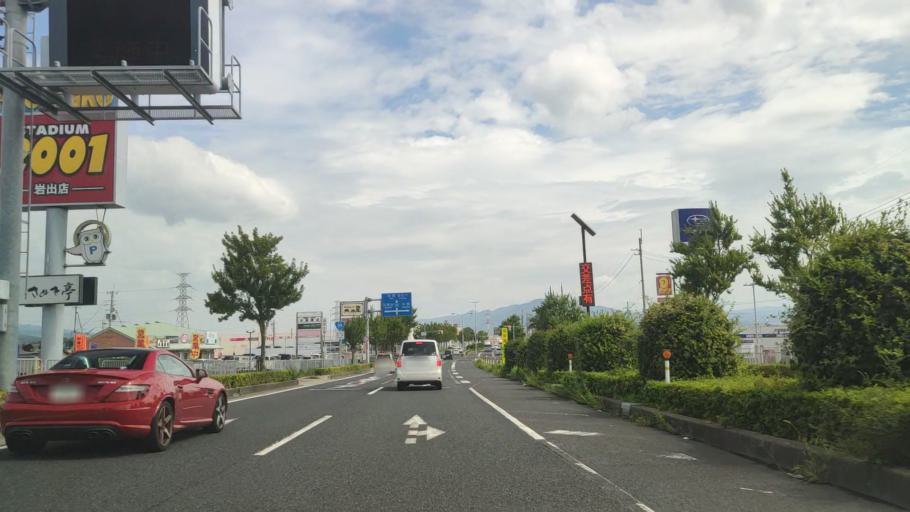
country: JP
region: Wakayama
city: Iwade
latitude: 34.2641
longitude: 135.2837
